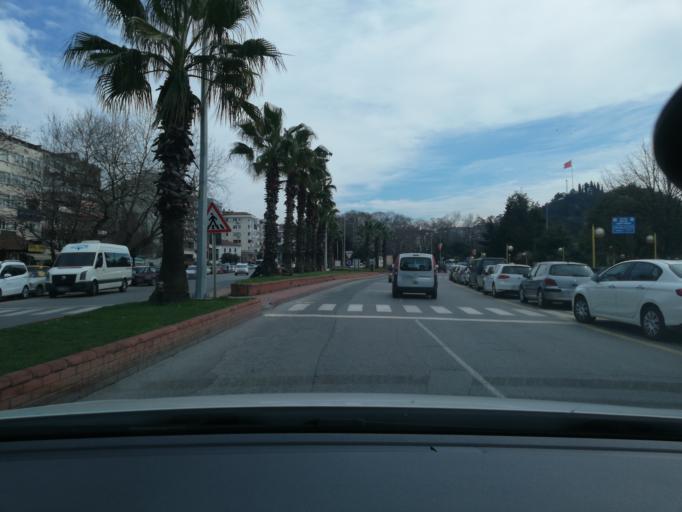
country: TR
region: Zonguldak
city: Eregli
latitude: 41.2803
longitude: 31.4189
